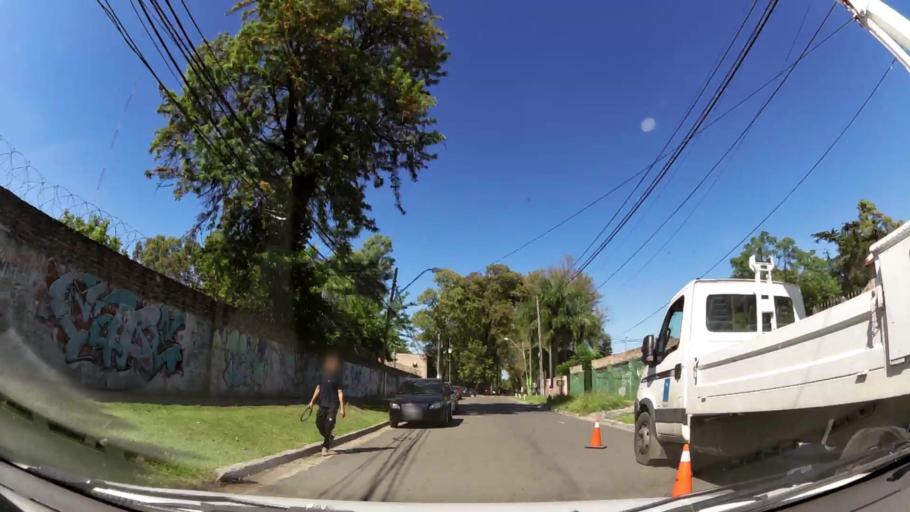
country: AR
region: Buenos Aires
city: Ituzaingo
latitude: -34.6242
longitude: -58.6602
